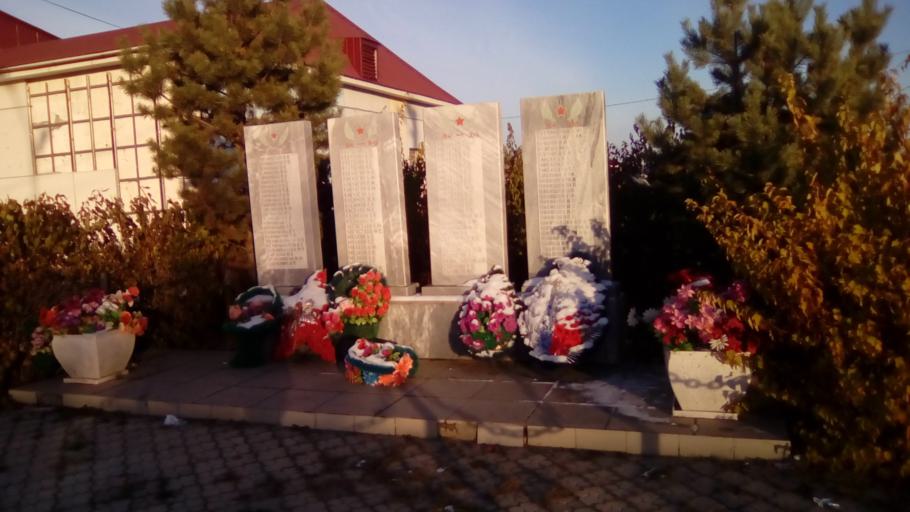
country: RU
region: Tjumen
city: Moskovskiy
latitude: 57.2215
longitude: 65.3595
